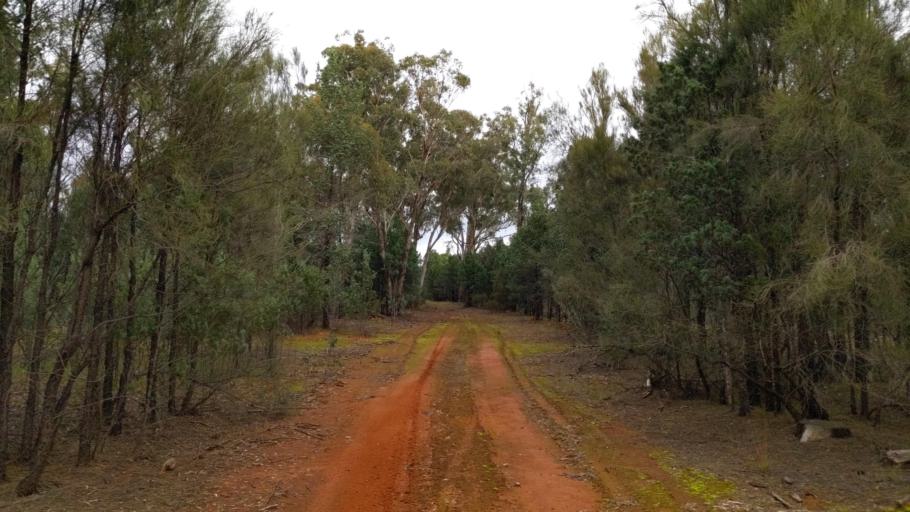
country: AU
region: New South Wales
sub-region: Coolamon
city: Coolamon
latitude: -34.8413
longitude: 146.9336
